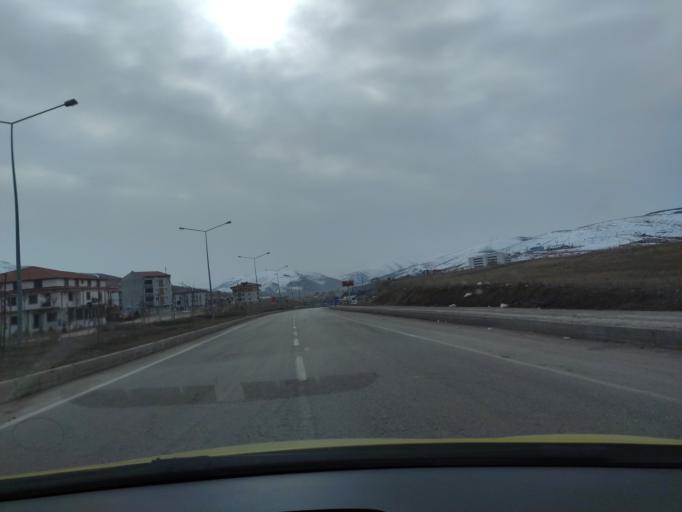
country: TR
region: Bayburt
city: Bayburt
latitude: 40.2648
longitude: 40.2047
